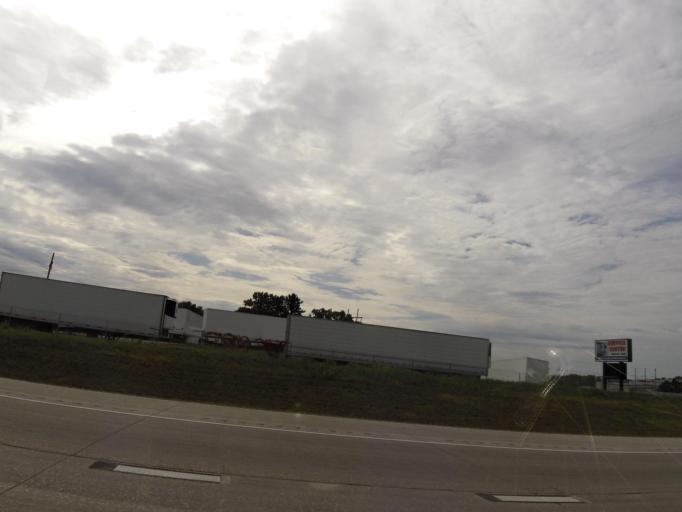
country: US
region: Wisconsin
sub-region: La Crosse County
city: Onalaska
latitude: 43.8695
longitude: -91.2209
